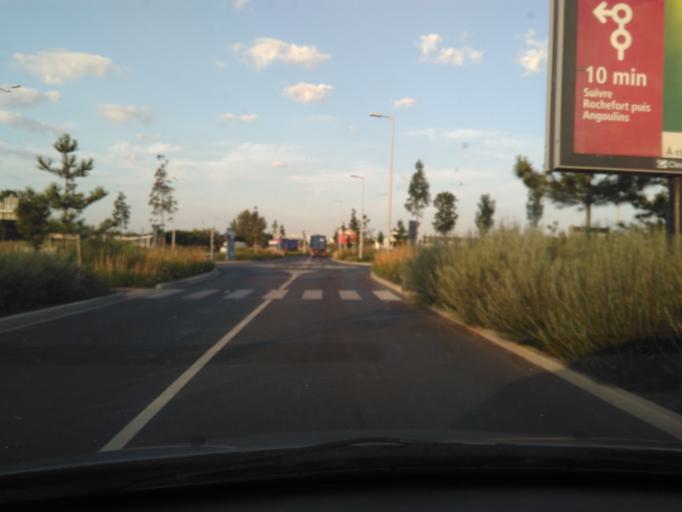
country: FR
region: Poitou-Charentes
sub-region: Departement de la Charente-Maritime
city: Puilboreau
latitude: 46.1747
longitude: -1.1152
